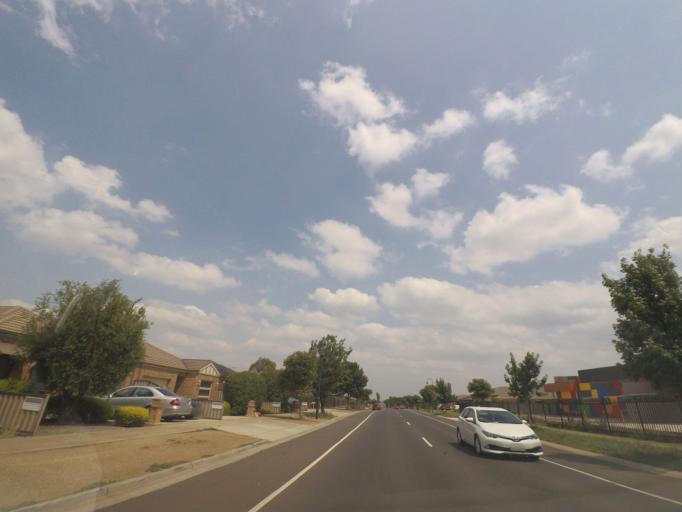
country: AU
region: Victoria
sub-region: Melton
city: Brookfield
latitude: -37.6930
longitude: 144.5549
